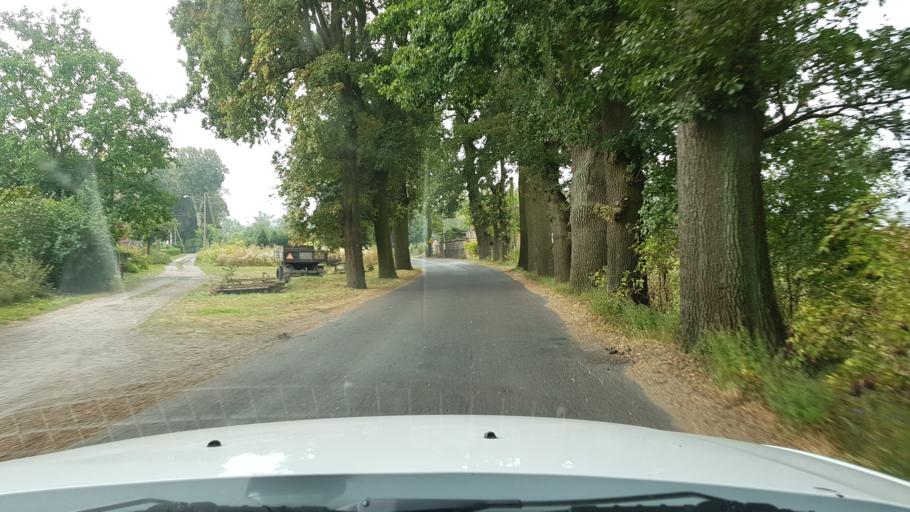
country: PL
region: West Pomeranian Voivodeship
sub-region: Powiat gryfinski
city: Moryn
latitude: 52.9007
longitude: 14.3753
